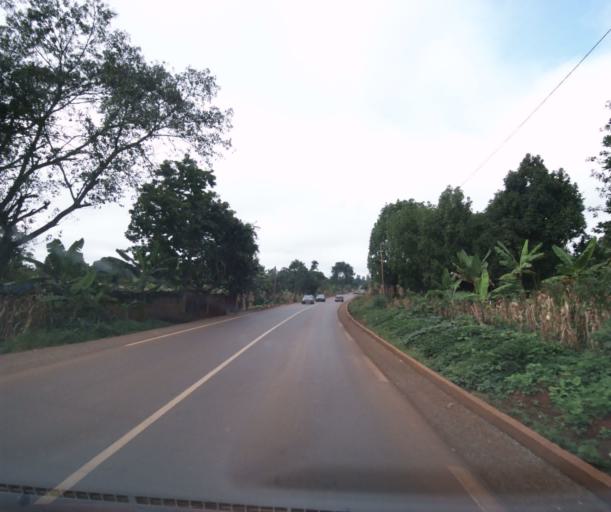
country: CM
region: West
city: Mbouda
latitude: 5.5855
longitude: 10.2976
